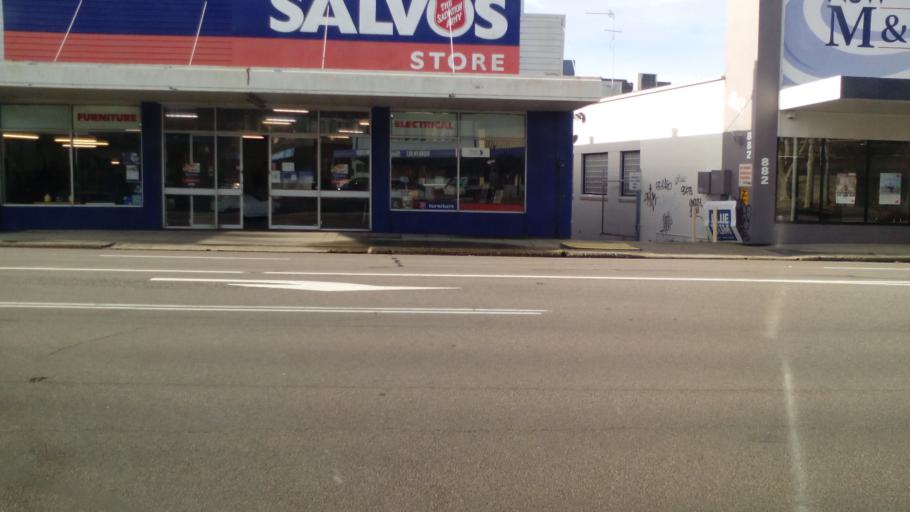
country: AU
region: New South Wales
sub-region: Newcastle
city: Hamilton
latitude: -32.9246
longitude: 151.7572
